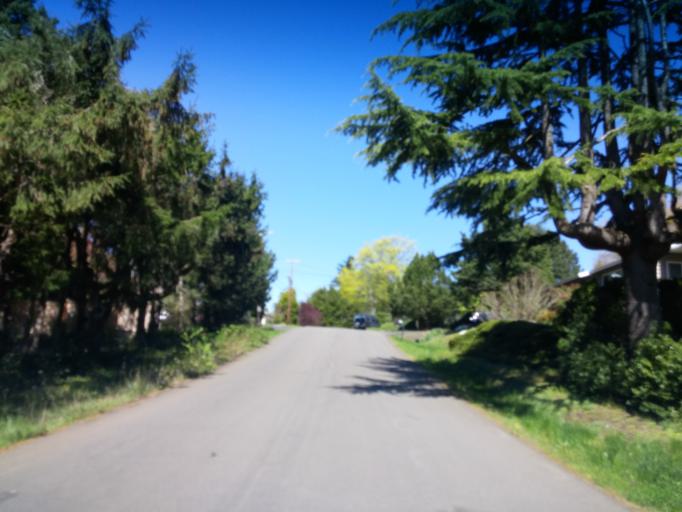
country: US
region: Oregon
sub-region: Washington County
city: West Haven
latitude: 45.5284
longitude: -122.7748
